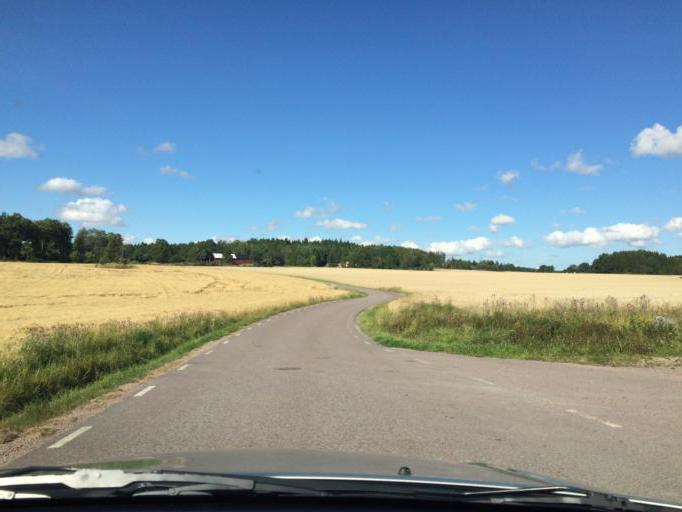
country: SE
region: Soedermanland
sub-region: Eskilstuna Kommun
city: Kvicksund
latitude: 59.5090
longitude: 16.4069
